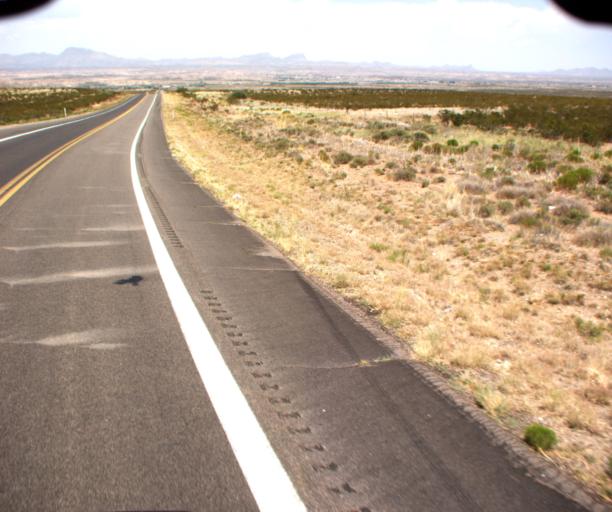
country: US
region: Arizona
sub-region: Greenlee County
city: Clifton
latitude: 32.7267
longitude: -109.1624
